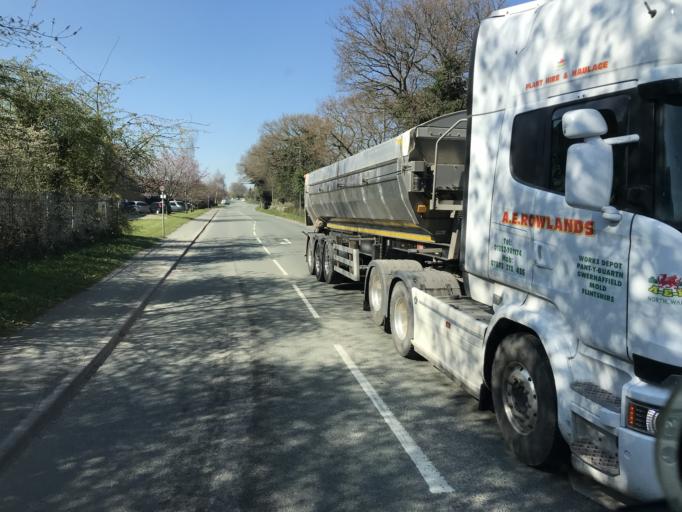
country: GB
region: Wales
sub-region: Wrexham
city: Gresford
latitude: 53.1000
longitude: -2.9984
